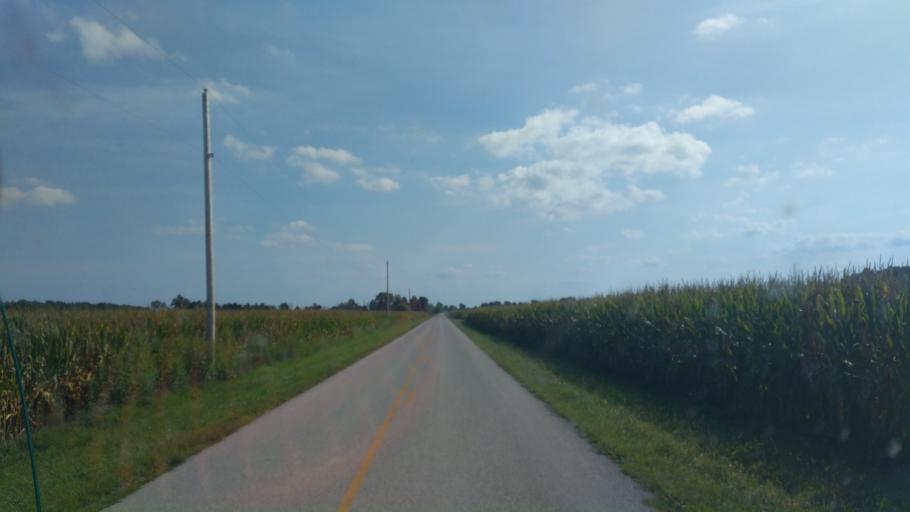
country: US
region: Ohio
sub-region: Hardin County
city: Forest
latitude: 40.7012
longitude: -83.5144
